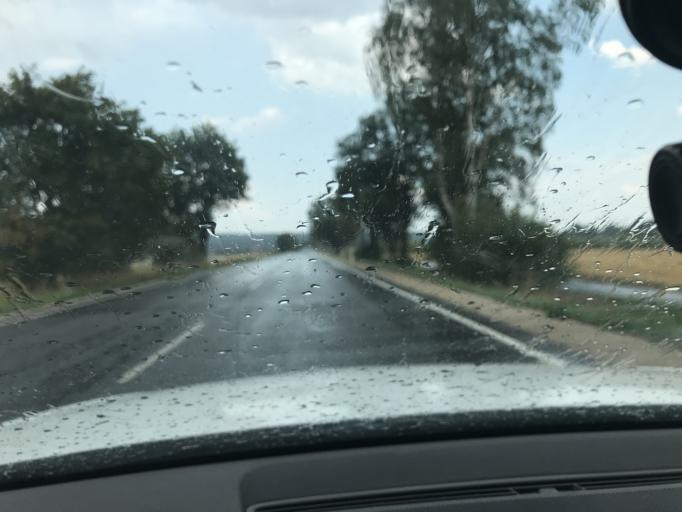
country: DE
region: Bavaria
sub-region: Upper Palatinate
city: Grafenwohr
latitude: 49.7336
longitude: 11.8878
